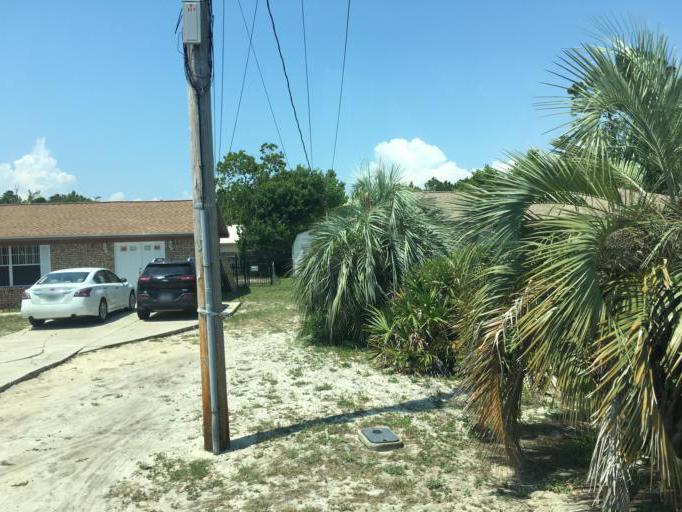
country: US
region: Florida
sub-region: Bay County
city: Laguna Beach
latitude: 30.2348
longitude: -85.8907
